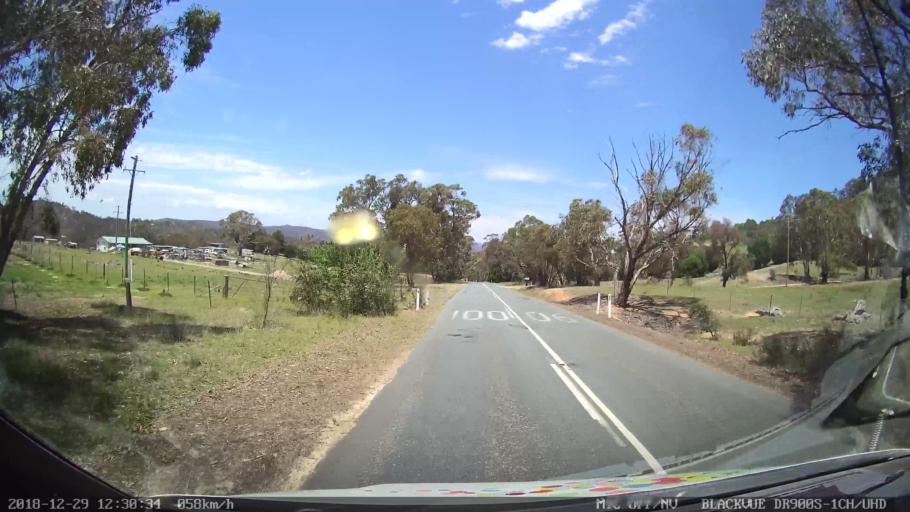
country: AU
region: Australian Capital Territory
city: Macarthur
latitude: -35.5070
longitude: 149.2329
